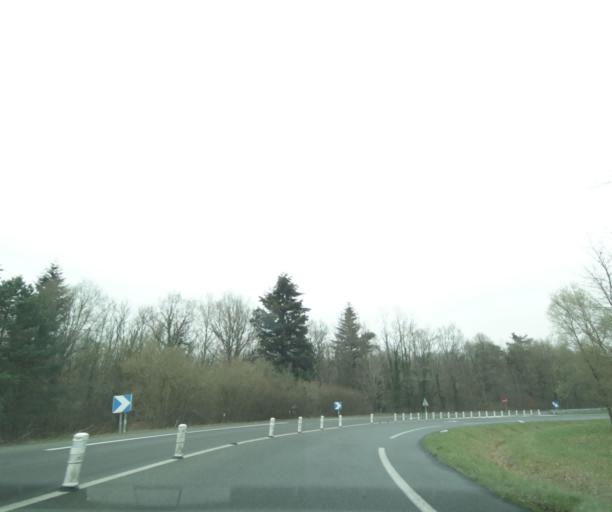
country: FR
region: Centre
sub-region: Departement du Loiret
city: Saint-Hilaire-Saint-Mesmin
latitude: 47.8421
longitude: 1.8636
